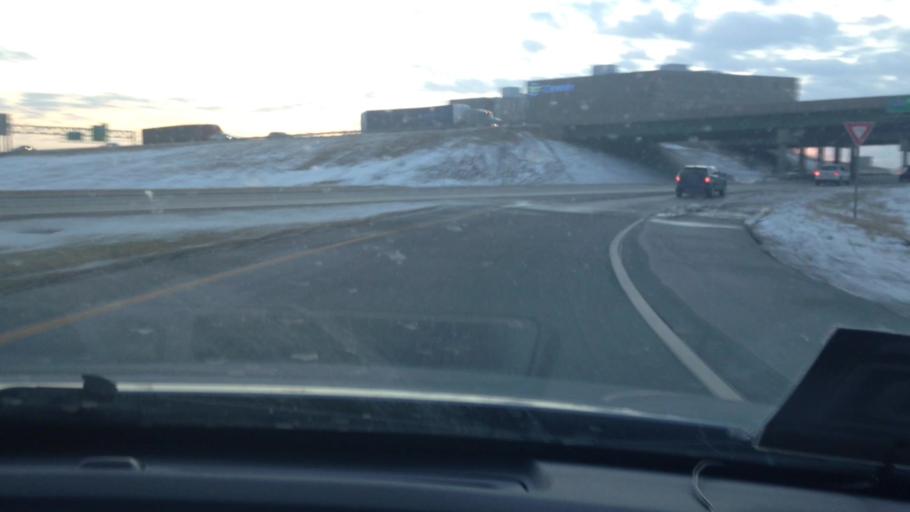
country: US
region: Kansas
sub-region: Wyandotte County
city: Edwardsville
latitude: 39.1172
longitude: -94.8093
